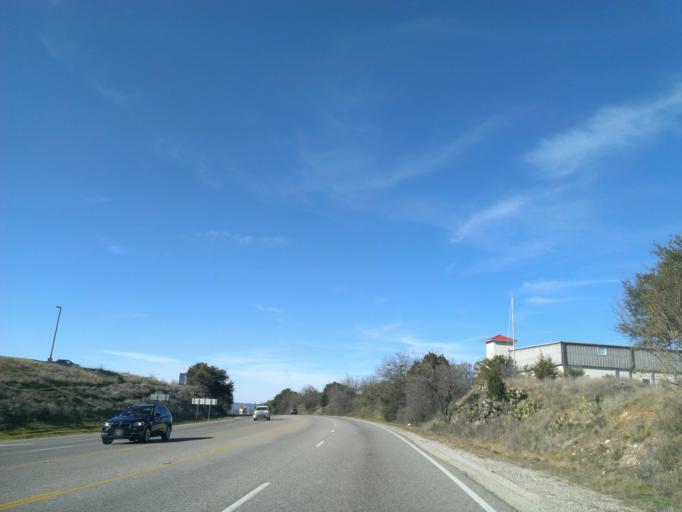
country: US
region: Texas
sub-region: Burnet County
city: Marble Falls
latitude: 30.5565
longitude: -98.2739
